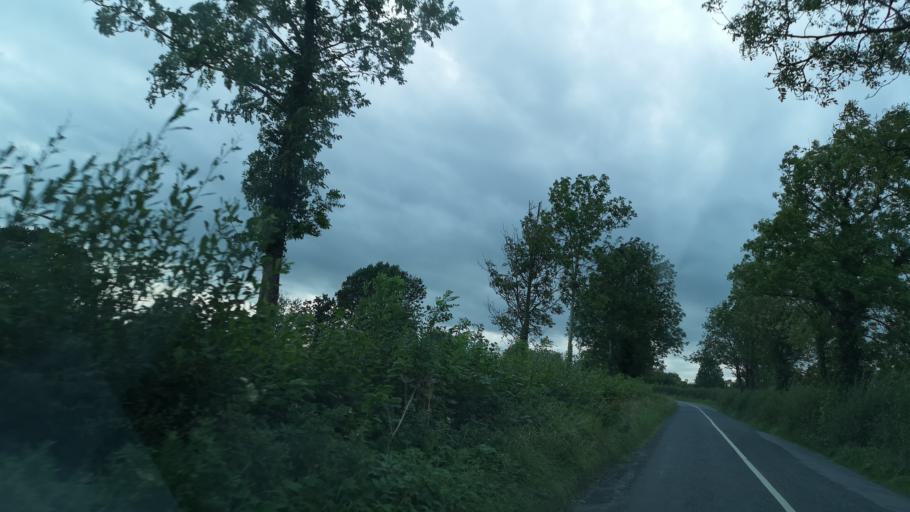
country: IE
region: Leinster
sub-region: Uibh Fhaili
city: Ferbane
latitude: 53.2226
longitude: -7.8157
